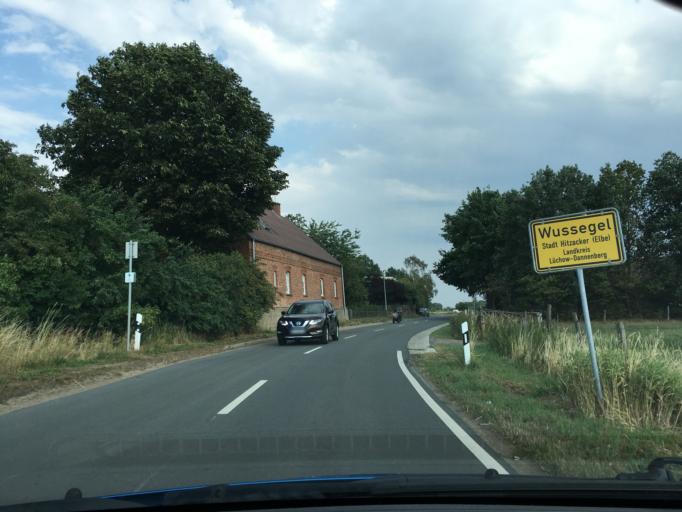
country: DE
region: Lower Saxony
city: Hitzacker
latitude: 53.1382
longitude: 11.0760
